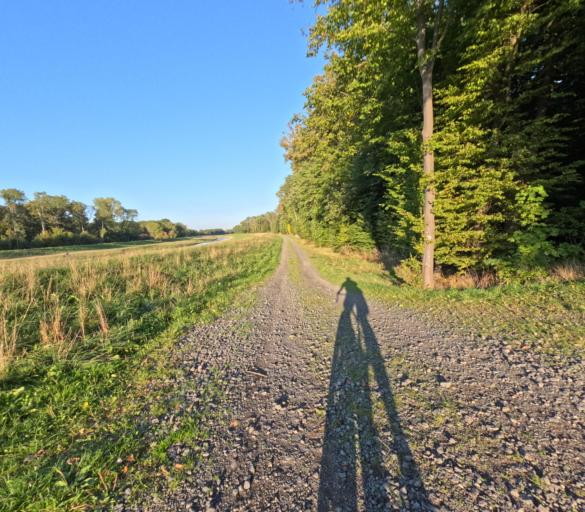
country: DE
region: Saxony
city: Schkeuditz
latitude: 51.3741
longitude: 12.2436
